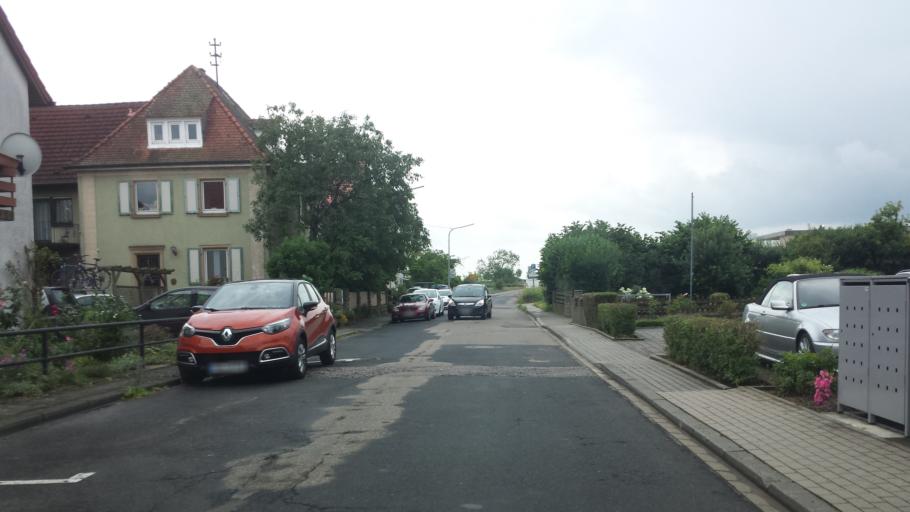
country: DE
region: Rheinland-Pfalz
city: Maikammer
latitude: 49.3168
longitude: 8.1356
